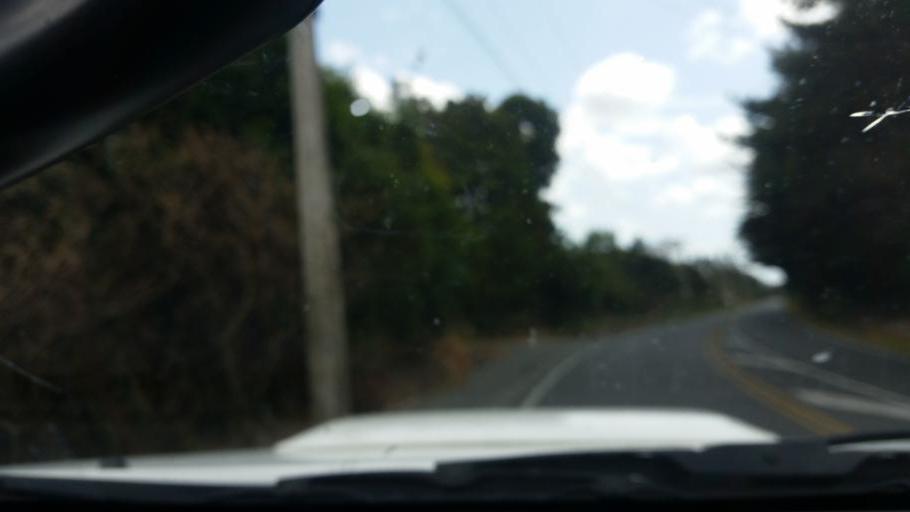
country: NZ
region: Auckland
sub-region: Auckland
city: Wellsford
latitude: -36.1221
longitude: 174.5719
